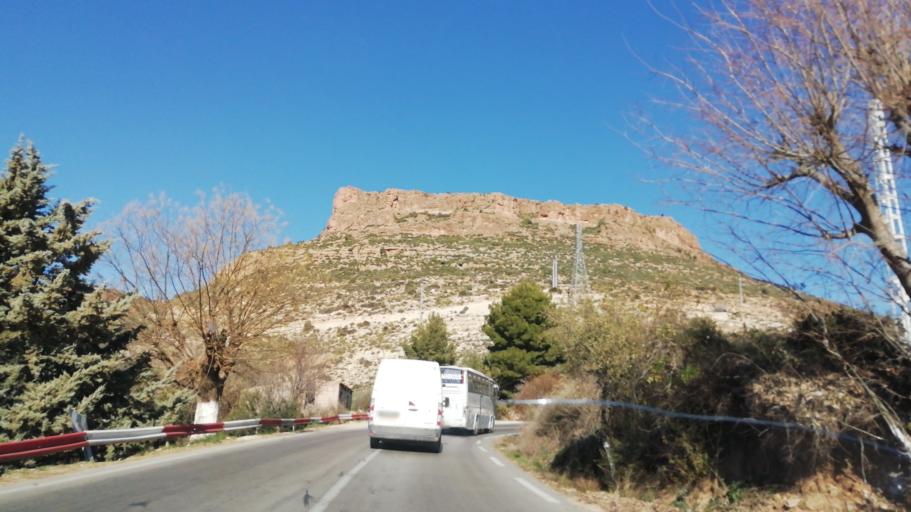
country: DZ
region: Tlemcen
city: Sebdou
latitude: 34.6862
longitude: -1.3184
